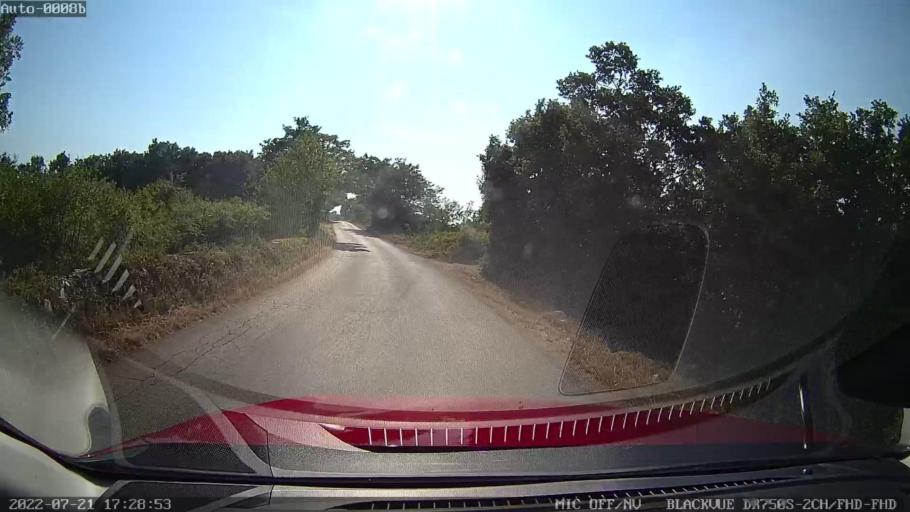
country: HR
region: Istarska
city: Karojba
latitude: 45.1809
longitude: 13.7908
